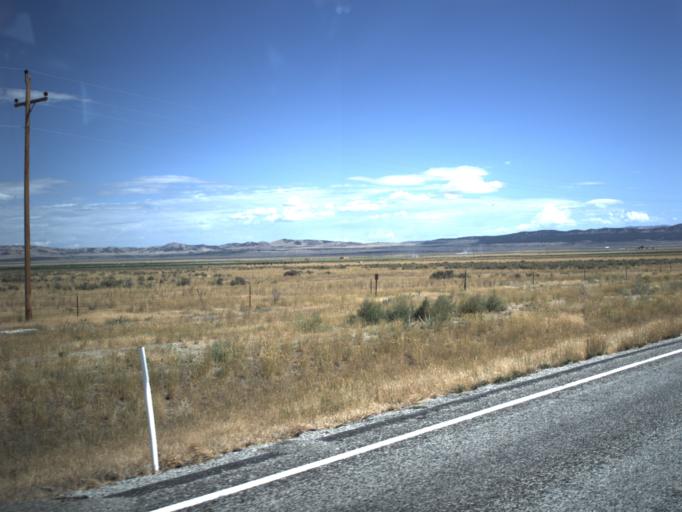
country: US
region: Idaho
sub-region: Oneida County
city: Malad City
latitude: 41.9662
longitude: -112.9546
